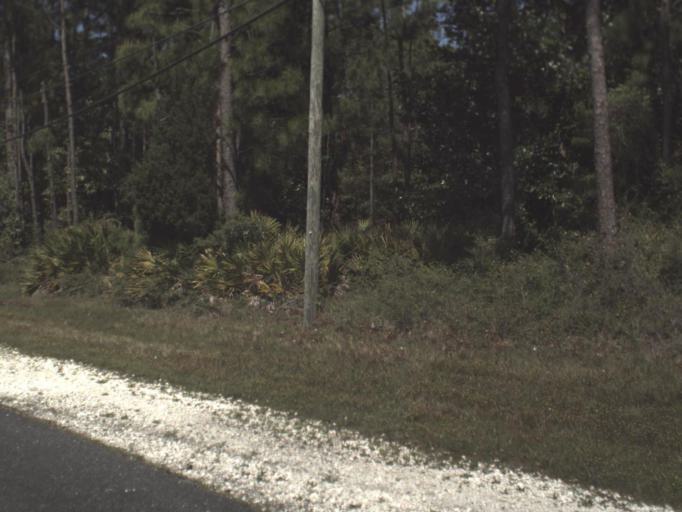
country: US
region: Florida
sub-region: Okaloosa County
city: Mary Esther
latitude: 30.4119
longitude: -86.7412
